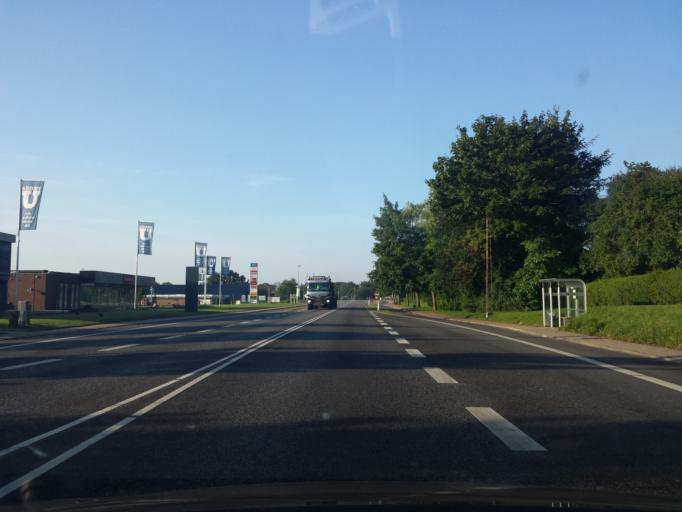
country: DK
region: South Denmark
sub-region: Sonderborg Kommune
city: Grasten
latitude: 54.9116
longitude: 9.5876
